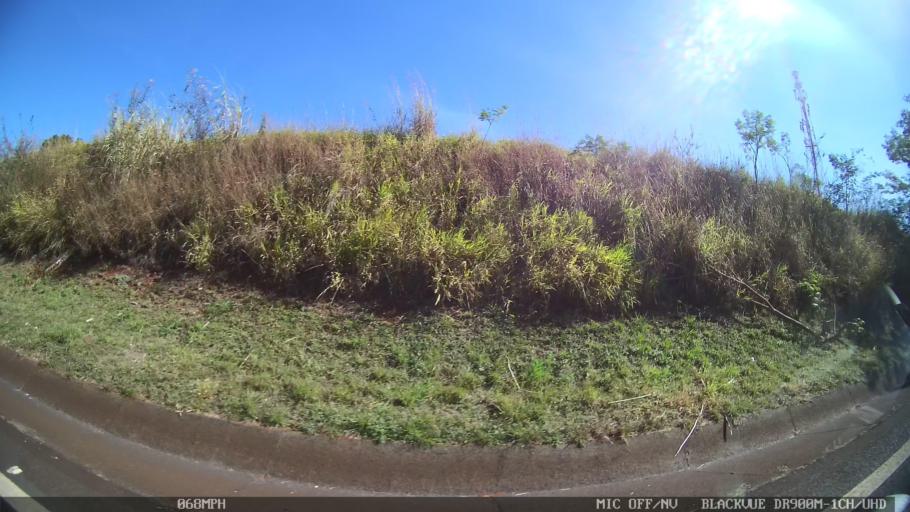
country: BR
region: Sao Paulo
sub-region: Cravinhos
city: Cravinhos
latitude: -21.3479
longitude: -47.7241
